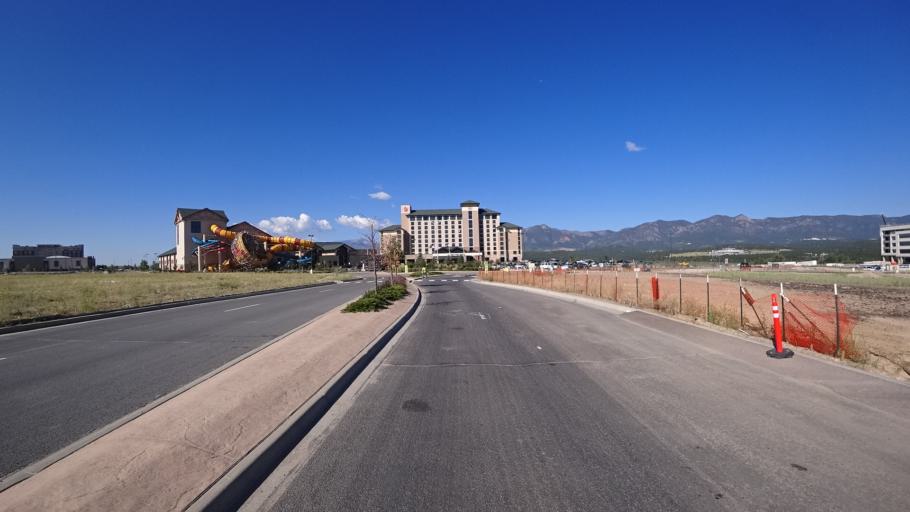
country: US
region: Colorado
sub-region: El Paso County
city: Gleneagle
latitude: 38.9972
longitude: -104.8093
